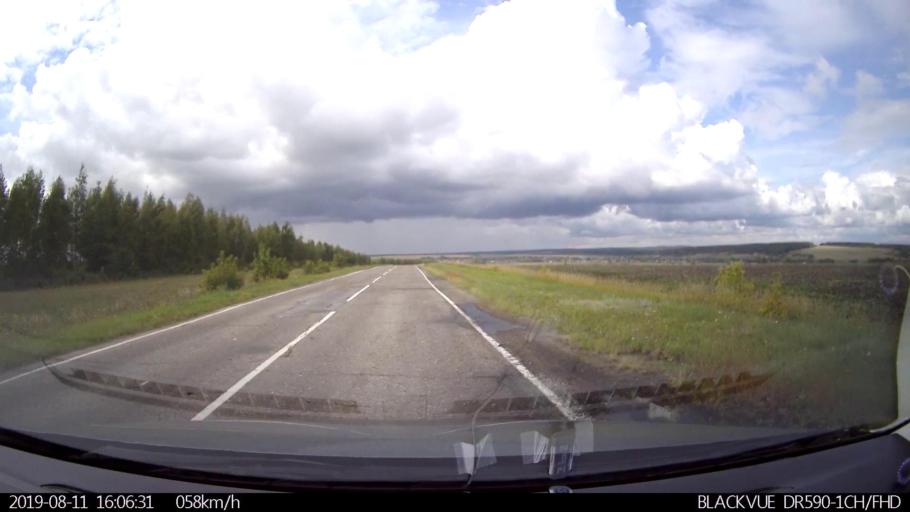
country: RU
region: Ulyanovsk
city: Ignatovka
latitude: 53.9695
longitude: 47.6483
